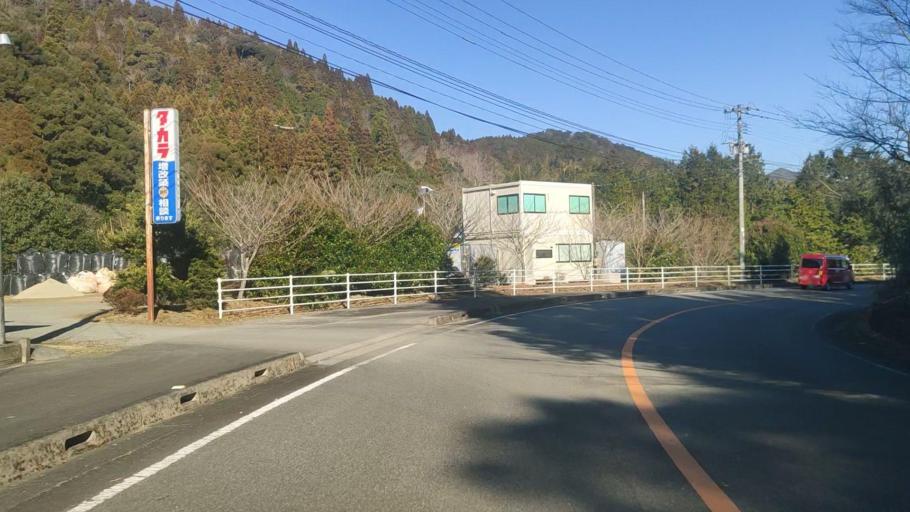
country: JP
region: Oita
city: Saiki
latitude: 32.7688
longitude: 131.8035
